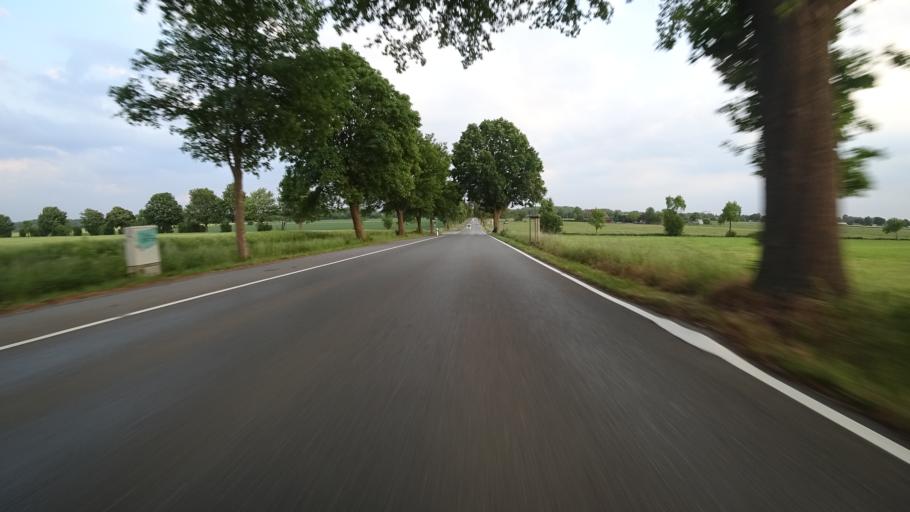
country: DE
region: North Rhine-Westphalia
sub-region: Regierungsbezirk Arnsberg
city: Lippstadt
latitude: 51.6444
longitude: 8.3576
